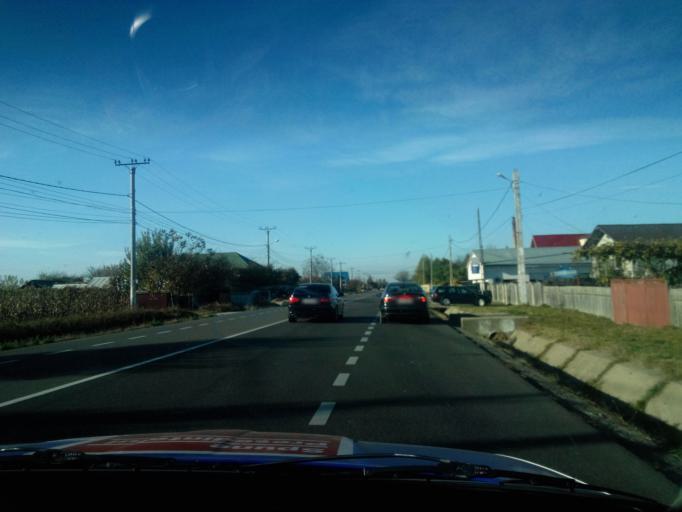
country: RO
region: Bacau
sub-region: Comuna Saucesti
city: Saucesti
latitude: 46.6121
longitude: 26.9248
